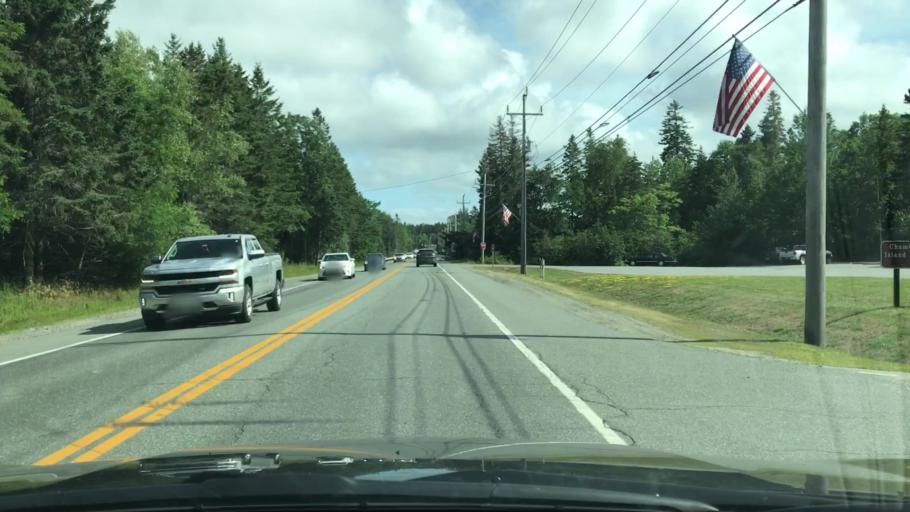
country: US
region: Maine
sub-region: Hancock County
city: Trenton
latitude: 44.4275
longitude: -68.3664
